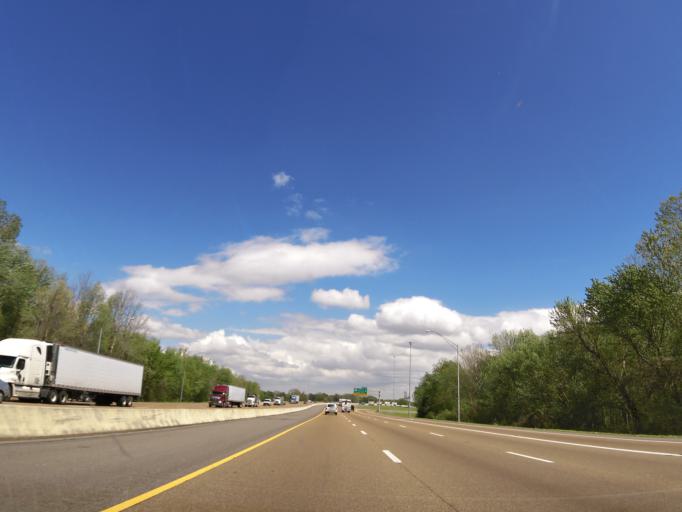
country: US
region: Tennessee
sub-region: Shelby County
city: Bartlett
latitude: 35.1913
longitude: -89.9342
